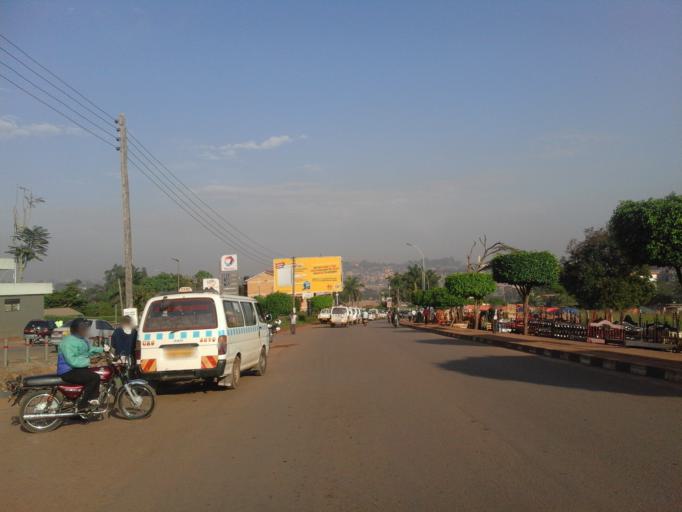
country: UG
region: Central Region
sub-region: Kampala District
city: Kampala
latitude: 0.3033
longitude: 32.5863
